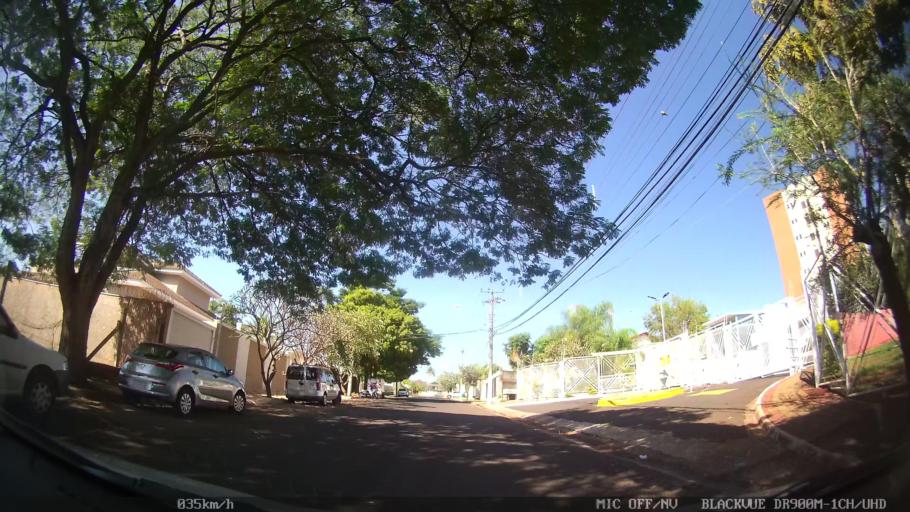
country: BR
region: Sao Paulo
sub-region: Ribeirao Preto
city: Ribeirao Preto
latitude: -21.2122
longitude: -47.7882
